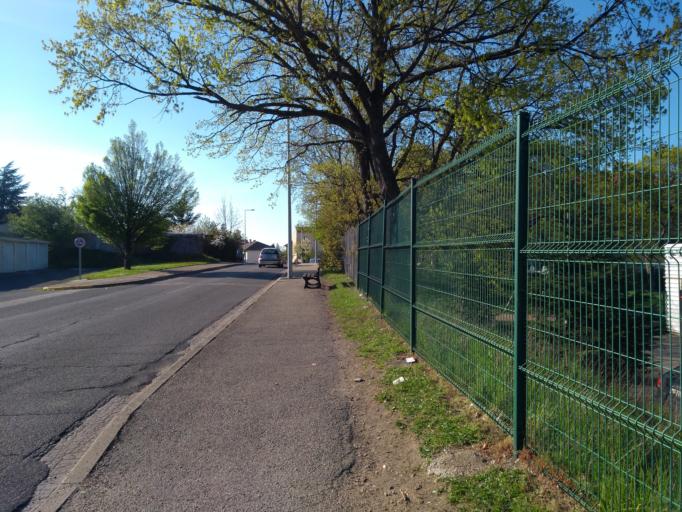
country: FR
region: Rhone-Alpes
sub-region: Departement de la Loire
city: Saint-Etienne
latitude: 45.4248
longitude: 4.4225
